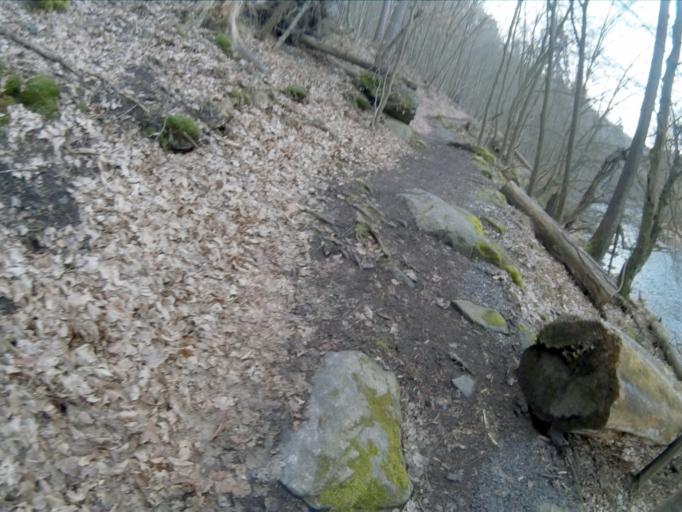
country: CZ
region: Vysocina
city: Namest' nad Oslavou
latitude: 49.1809
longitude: 16.1609
